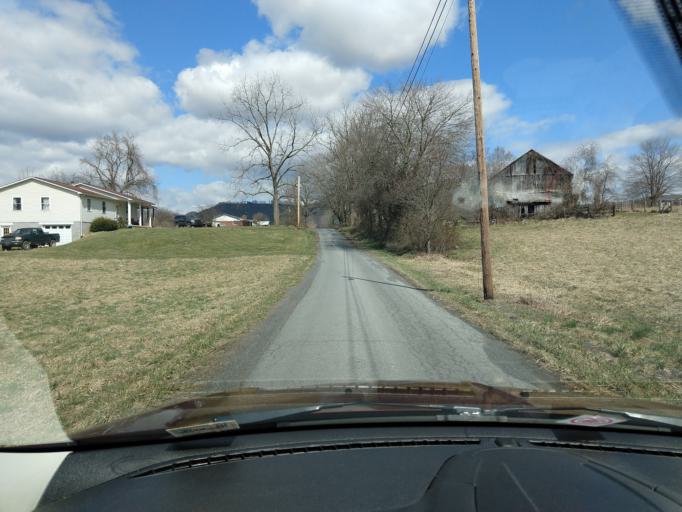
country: US
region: West Virginia
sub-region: Greenbrier County
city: Fairlea
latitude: 37.8189
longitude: -80.5604
